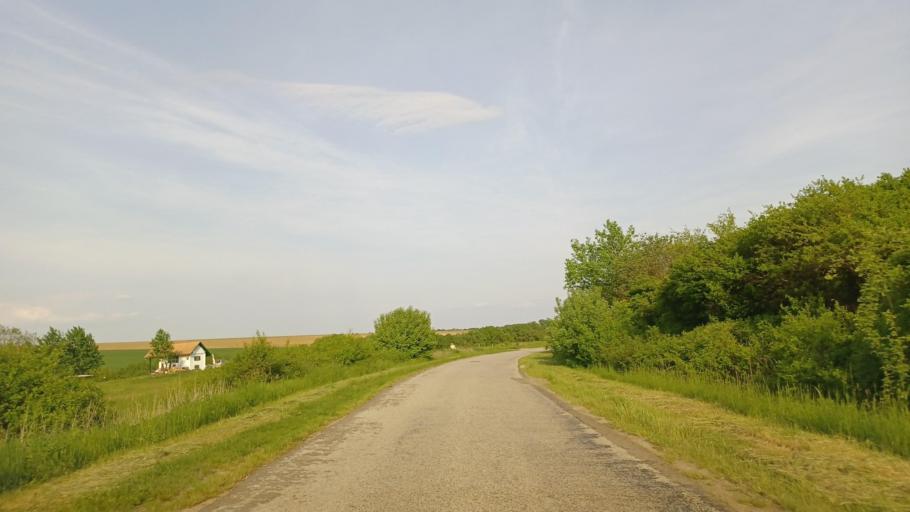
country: HU
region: Baranya
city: Kozarmisleny
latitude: 45.9634
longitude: 18.3727
